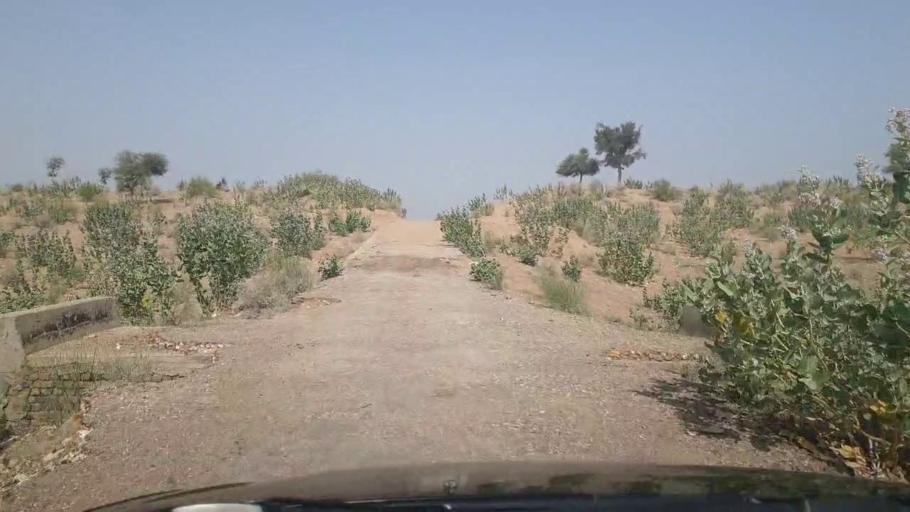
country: PK
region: Sindh
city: Islamkot
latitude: 25.0572
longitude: 70.2108
